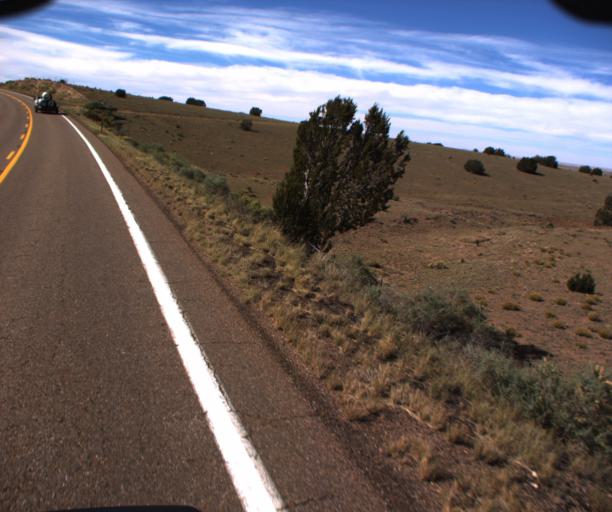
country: US
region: Arizona
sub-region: Apache County
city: Saint Johns
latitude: 34.4857
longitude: -109.5770
